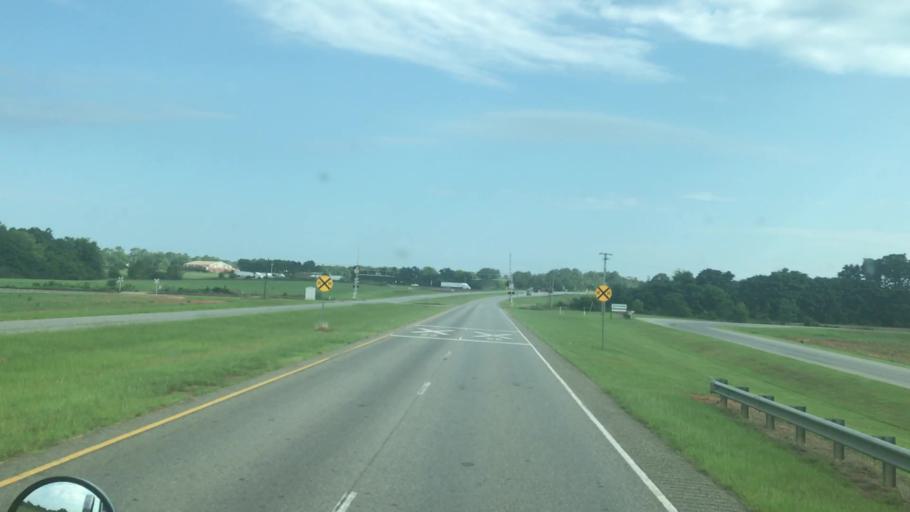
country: US
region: Georgia
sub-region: Early County
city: Blakely
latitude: 31.3866
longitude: -84.9225
